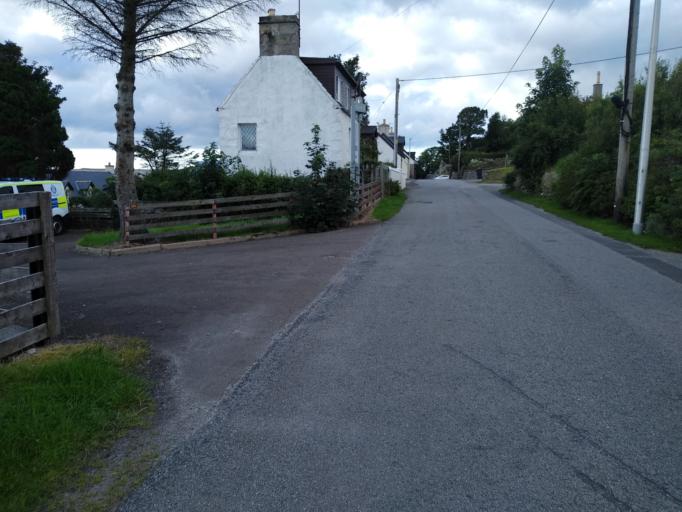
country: GB
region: Scotland
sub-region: Highland
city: Golspie
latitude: 58.4744
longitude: -4.4166
